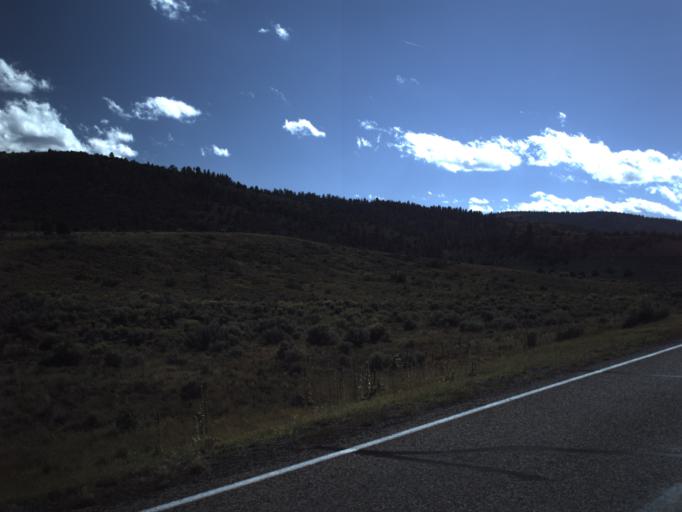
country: US
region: Utah
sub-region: Garfield County
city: Panguitch
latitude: 37.7661
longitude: -112.5517
